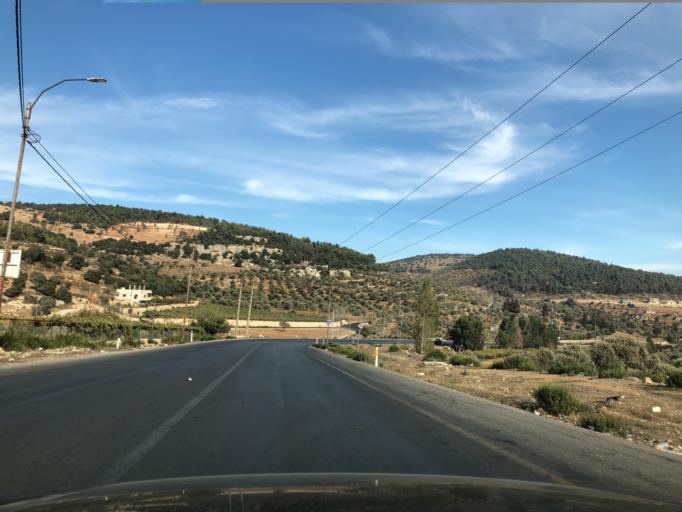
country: JO
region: Irbid
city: `Anjarah
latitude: 32.2985
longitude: 35.7835
